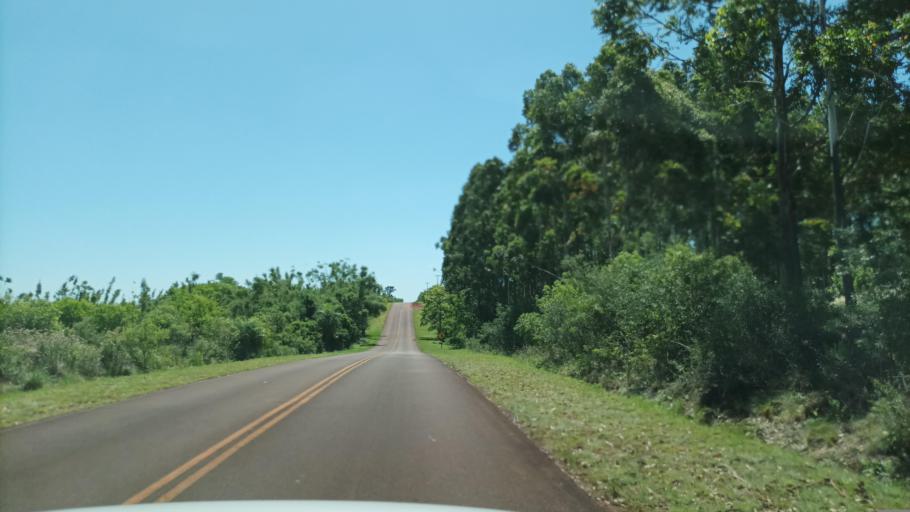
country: AR
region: Misiones
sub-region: Departamento de Apostoles
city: San Jose
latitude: -27.7736
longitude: -55.7503
